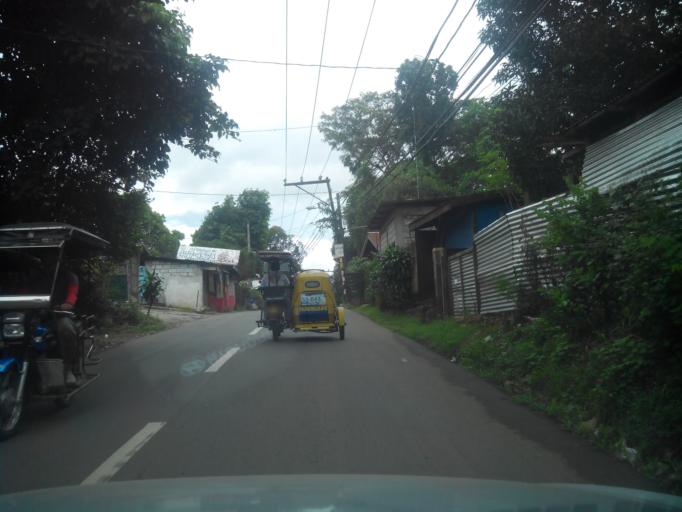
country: PH
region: Calabarzon
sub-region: Province of Rizal
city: Teresa
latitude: 14.5982
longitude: 121.1815
